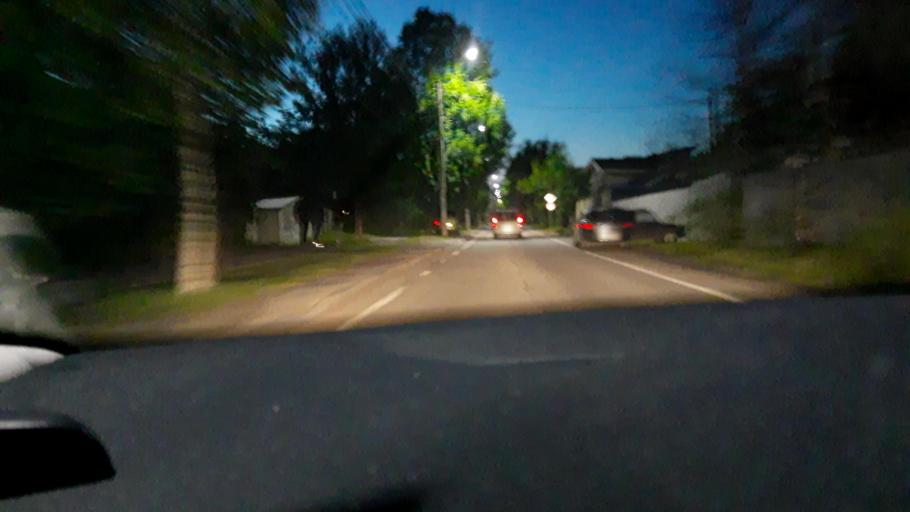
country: RU
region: Moskovskaya
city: Opalikha
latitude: 55.8252
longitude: 37.2464
